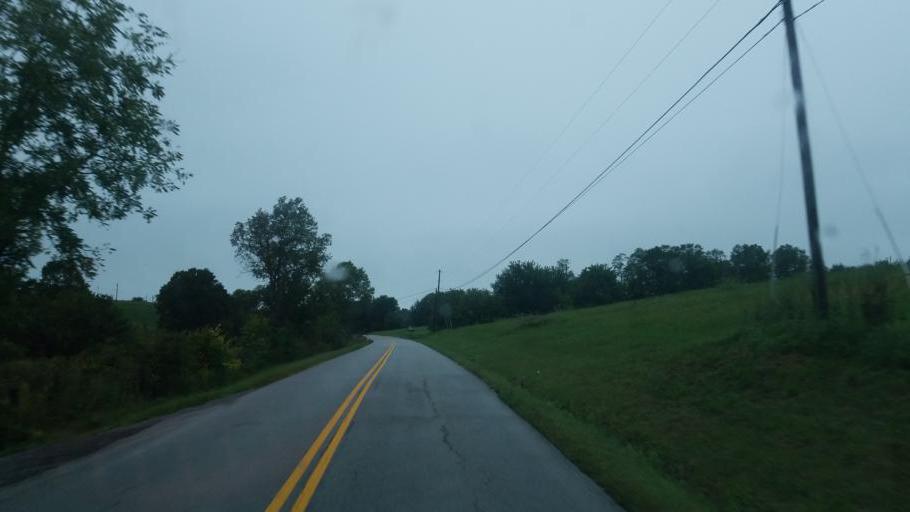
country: US
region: Kentucky
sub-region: Fleming County
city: Flemingsburg
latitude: 38.4238
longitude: -83.7065
